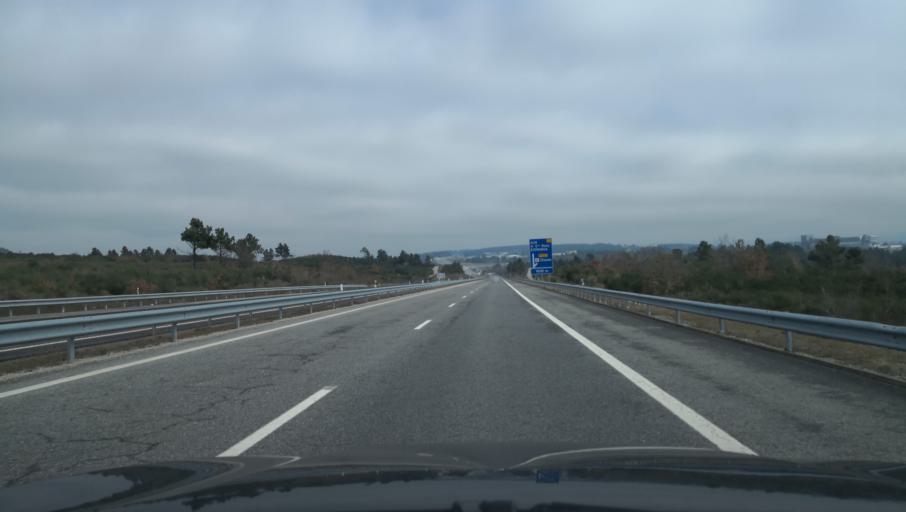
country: PT
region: Vila Real
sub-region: Chaves
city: Chaves
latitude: 41.7585
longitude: -7.5100
